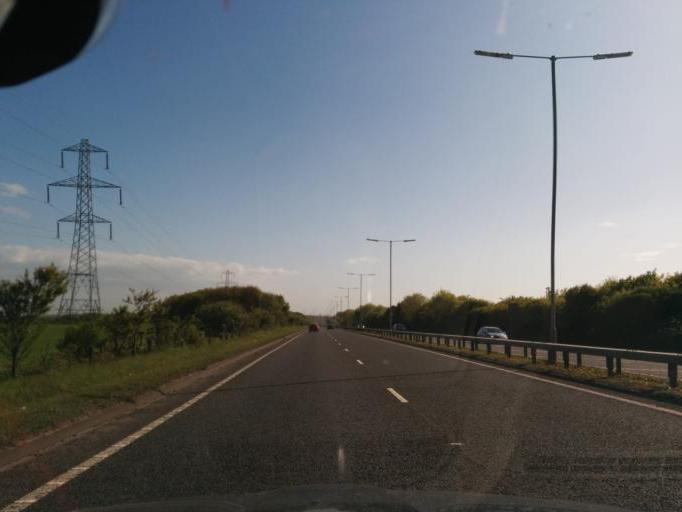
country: GB
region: England
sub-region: Northumberland
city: Newbiggin-by-the-Sea
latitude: 55.1674
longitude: -1.5347
